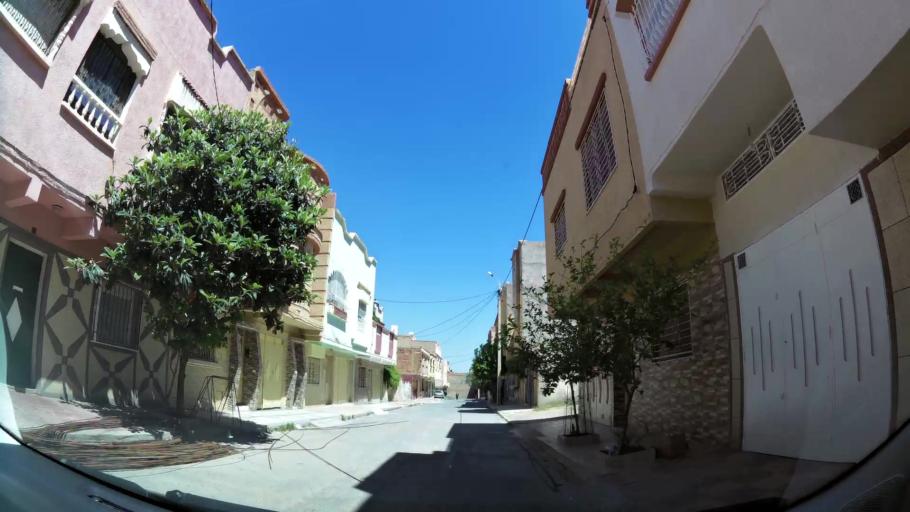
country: MA
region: Oriental
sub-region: Oujda-Angad
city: Oujda
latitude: 34.6637
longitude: -1.8833
